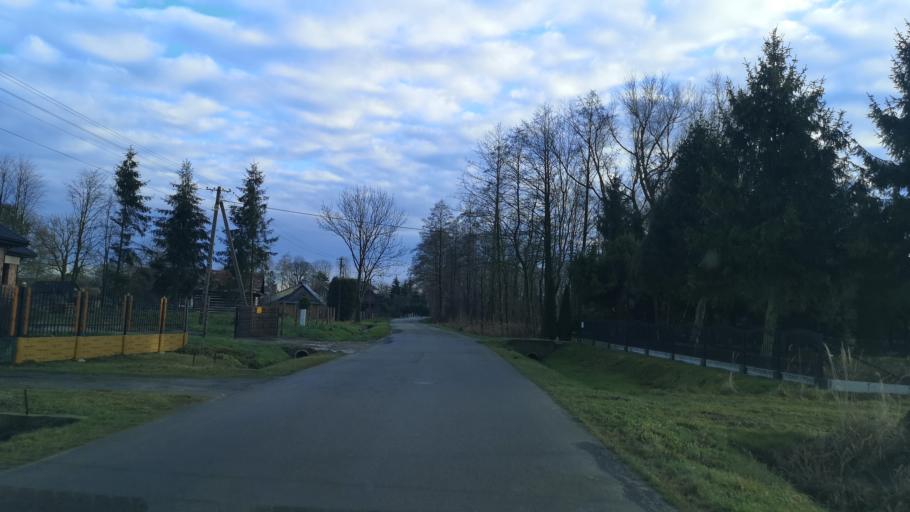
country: PL
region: Subcarpathian Voivodeship
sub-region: Powiat lezajski
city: Piskorowice
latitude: 50.2611
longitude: 22.5950
